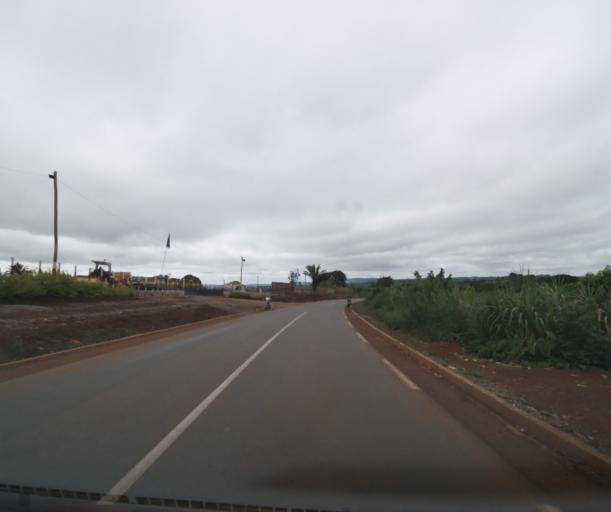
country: CM
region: West
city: Bansoa
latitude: 5.5456
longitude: 10.3285
